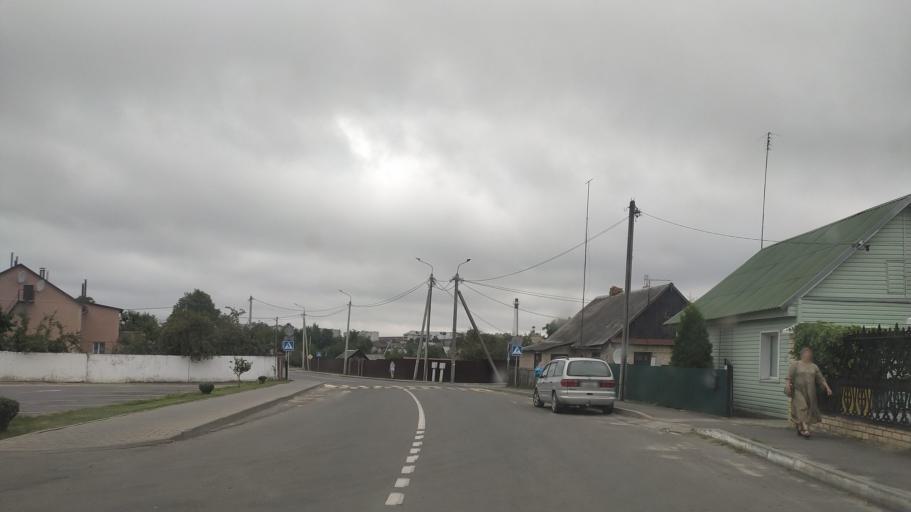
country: BY
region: Brest
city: Byaroza
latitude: 52.5362
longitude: 24.9782
